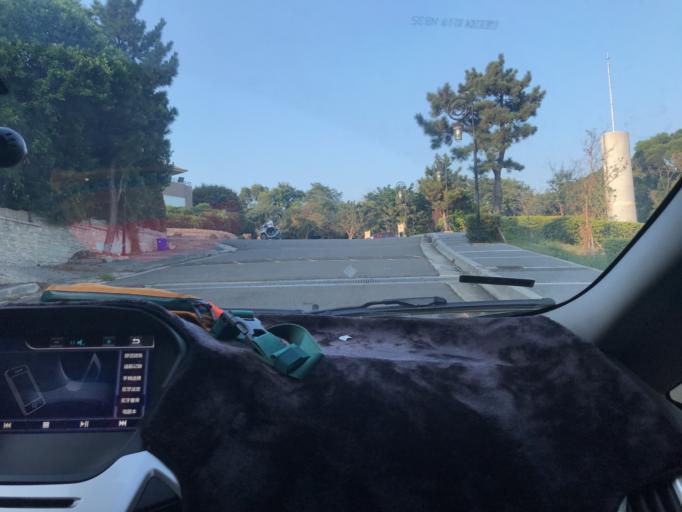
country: TW
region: Taiwan
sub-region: Hsinchu
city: Zhubei
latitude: 24.8473
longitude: 121.0377
